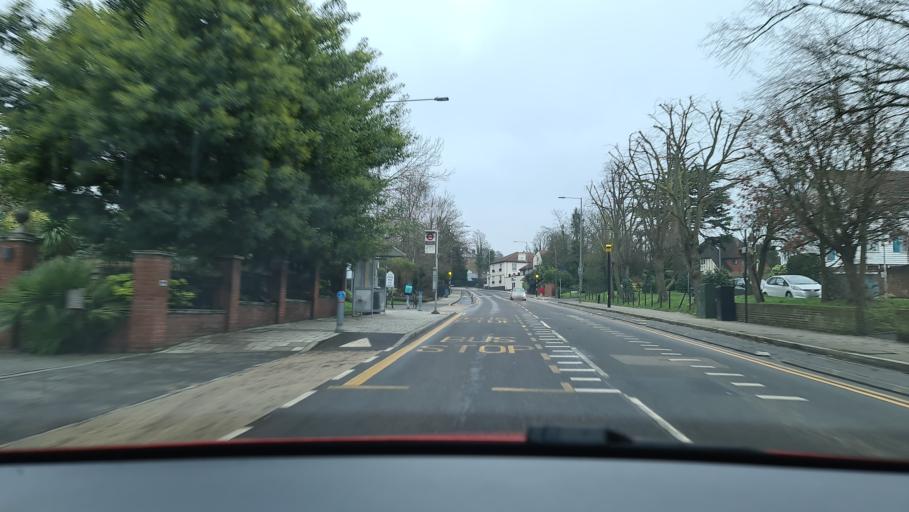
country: GB
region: England
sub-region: Greater London
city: Kingston upon Thames
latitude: 51.4179
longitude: -0.2809
